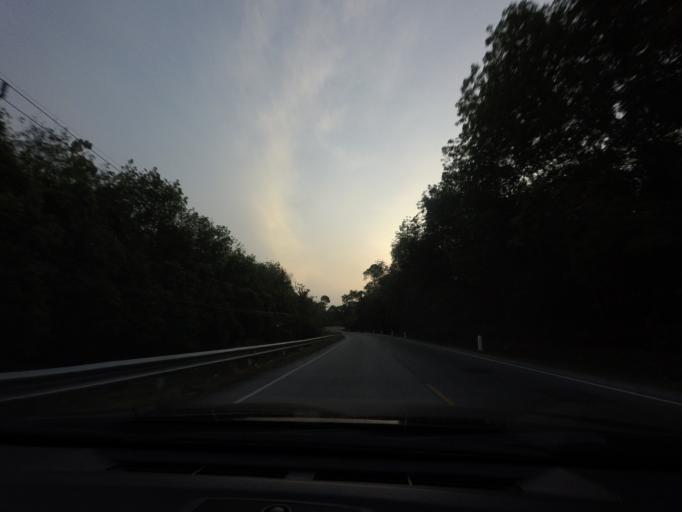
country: TH
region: Narathiwat
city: Rueso
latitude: 6.3603
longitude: 101.5877
